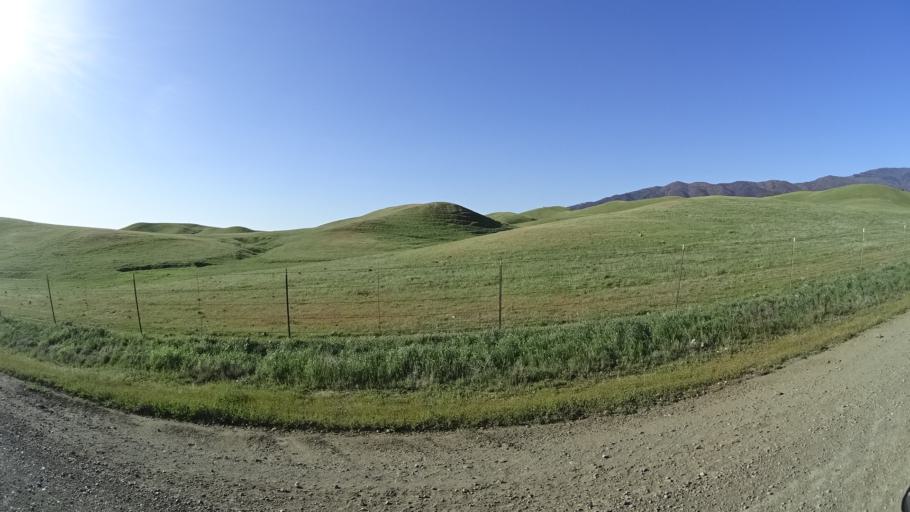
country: US
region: California
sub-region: Tehama County
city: Rancho Tehama Reserve
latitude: 39.7988
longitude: -122.5569
